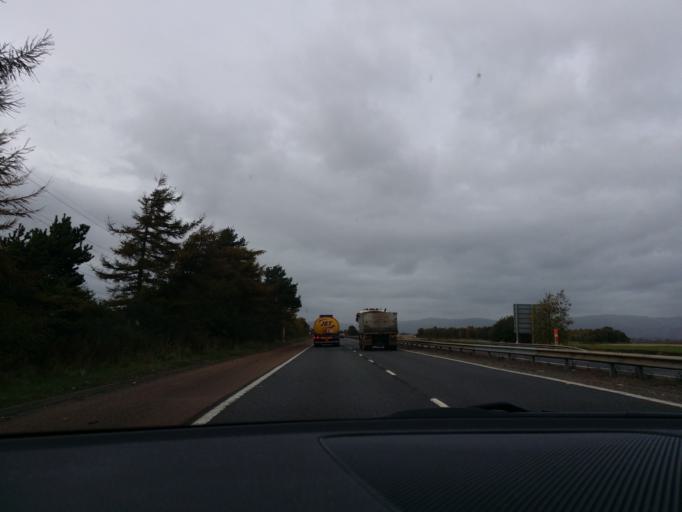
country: GB
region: Scotland
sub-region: Falkirk
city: Airth
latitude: 56.0317
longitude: -3.7653
